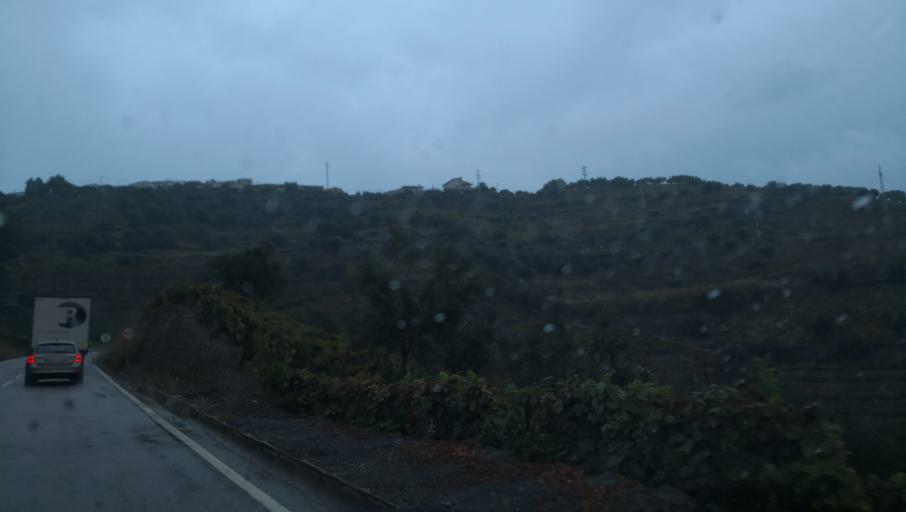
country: PT
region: Vila Real
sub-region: Santa Marta de Penaguiao
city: Santa Marta de Penaguiao
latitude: 41.2228
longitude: -7.7315
